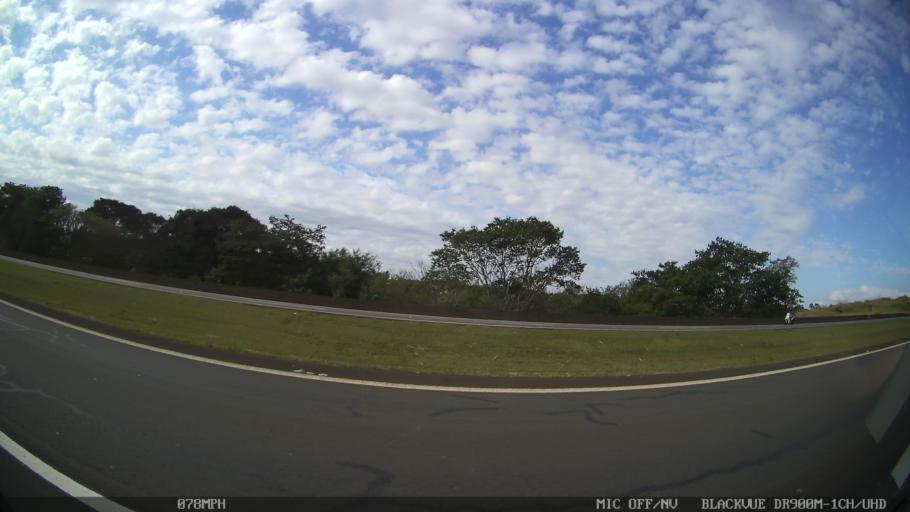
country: BR
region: Sao Paulo
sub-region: Iracemapolis
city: Iracemapolis
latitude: -22.6282
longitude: -47.4574
